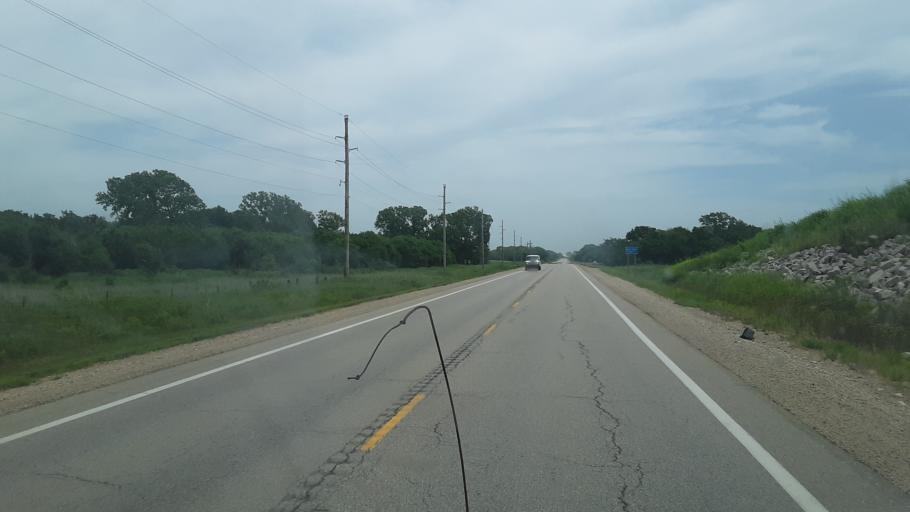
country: US
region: Kansas
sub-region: Woodson County
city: Yates Center
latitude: 37.8369
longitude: -95.9938
